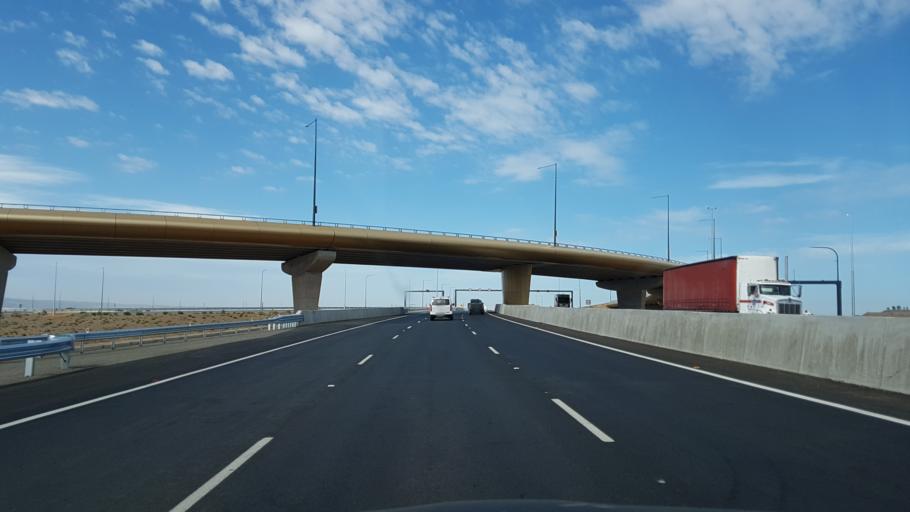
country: AU
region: South Australia
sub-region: Port Adelaide Enfield
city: Blair Athol
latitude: -34.8281
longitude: 138.5628
